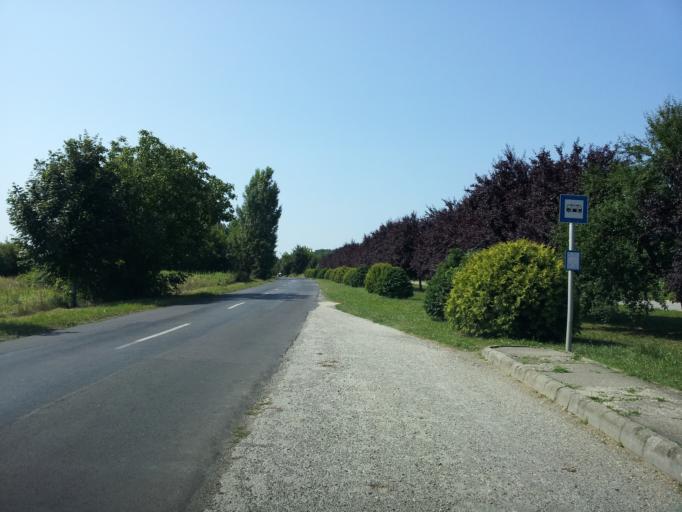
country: HU
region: Zala
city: Heviz
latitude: 46.8364
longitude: 17.0929
